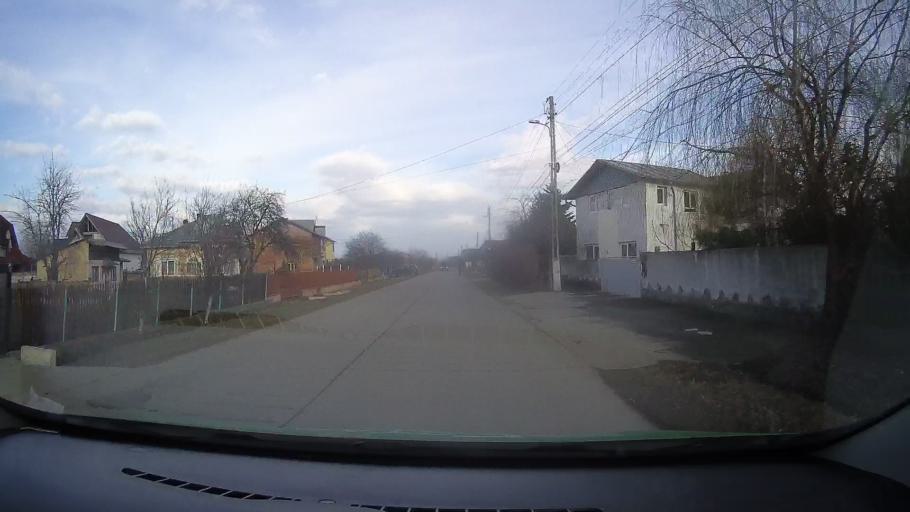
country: RO
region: Dambovita
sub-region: Comuna Vacaresti
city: Vacaresti
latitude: 44.8575
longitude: 25.4931
